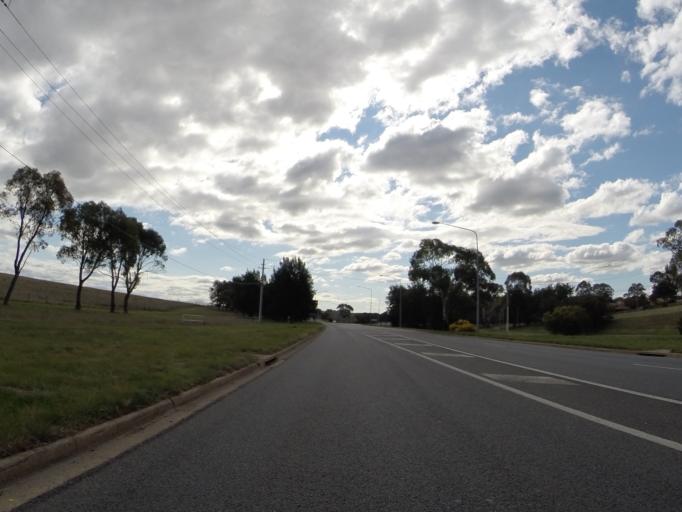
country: AU
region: Australian Capital Territory
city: Kaleen
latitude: -35.2201
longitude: 149.0987
